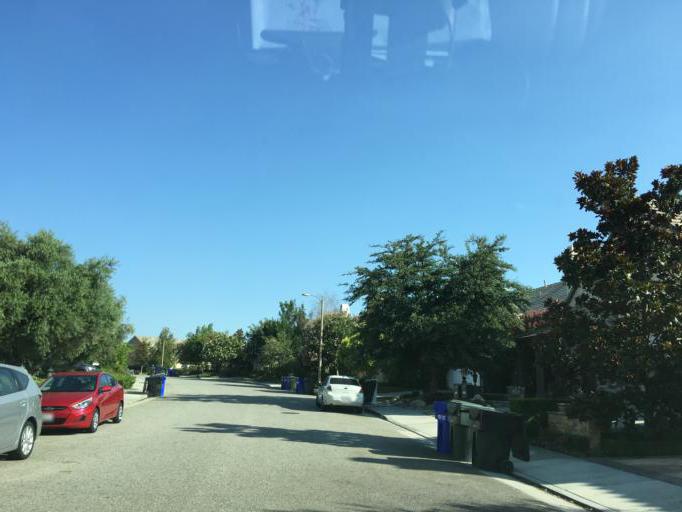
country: US
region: California
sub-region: Los Angeles County
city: Santa Clarita
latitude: 34.4085
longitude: -118.5829
